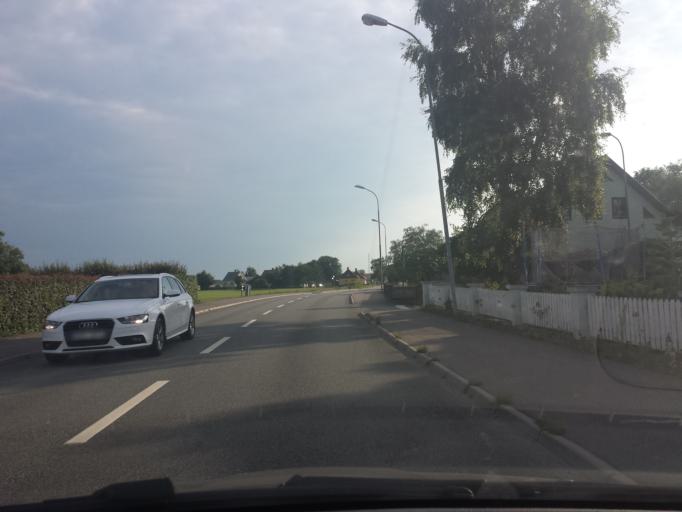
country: SE
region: Skane
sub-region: Ystads Kommun
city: Kopingebro
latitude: 55.4497
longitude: 14.0196
